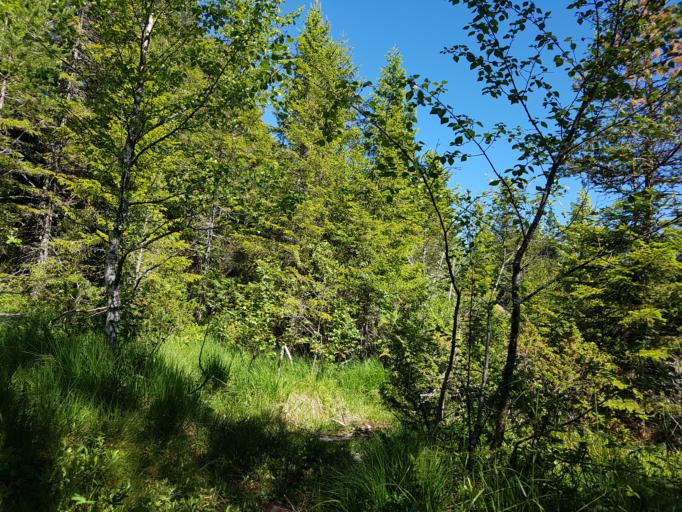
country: NO
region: Sor-Trondelag
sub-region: Melhus
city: Melhus
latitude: 63.4382
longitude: 10.2124
